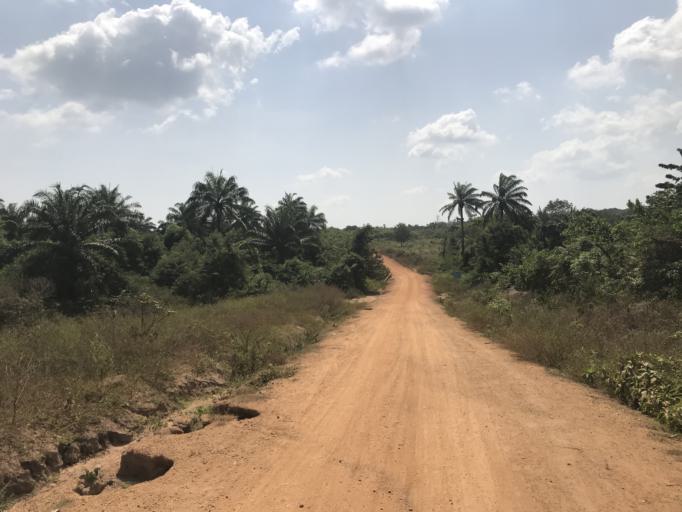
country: NG
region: Osun
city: Ifon
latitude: 7.9914
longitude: 4.5167
